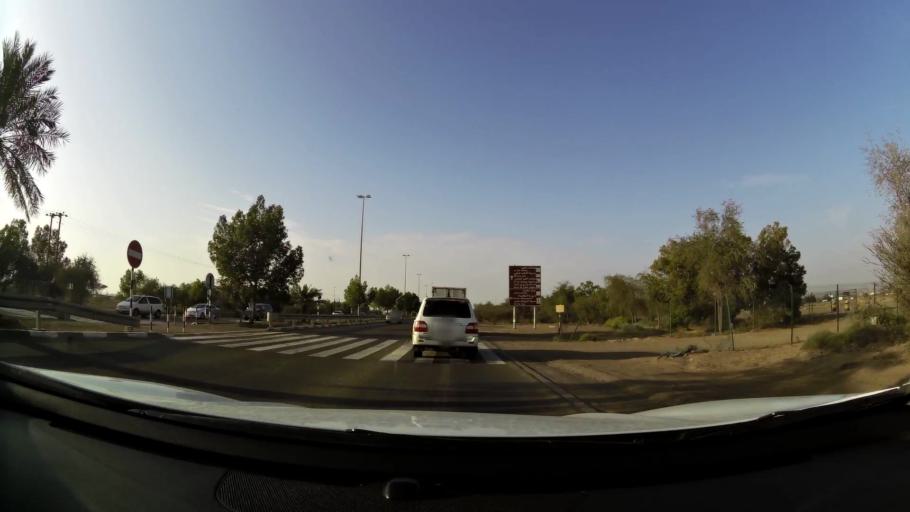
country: AE
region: Abu Dhabi
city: Al Ain
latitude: 24.1075
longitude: 55.8265
